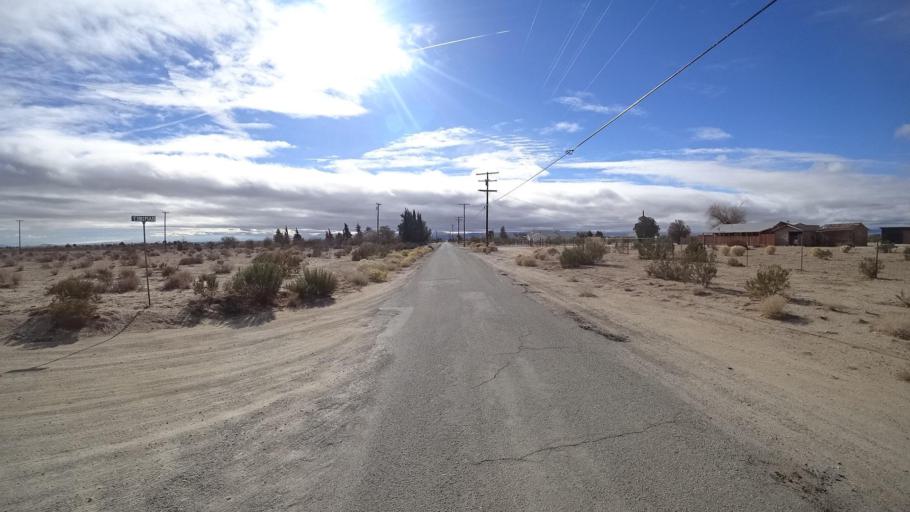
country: US
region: California
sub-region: Kern County
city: Rosamond
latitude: 34.8745
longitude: -118.2203
